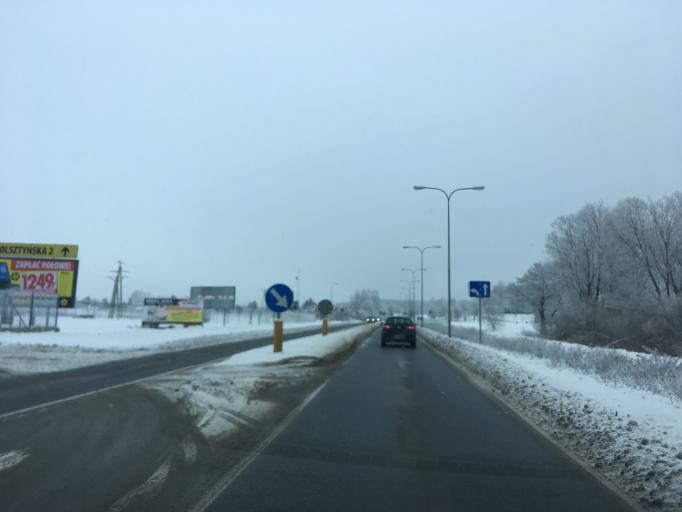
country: PL
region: Warmian-Masurian Voivodeship
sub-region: Powiat dzialdowski
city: Dzialdowo
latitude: 53.2402
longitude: 20.1773
